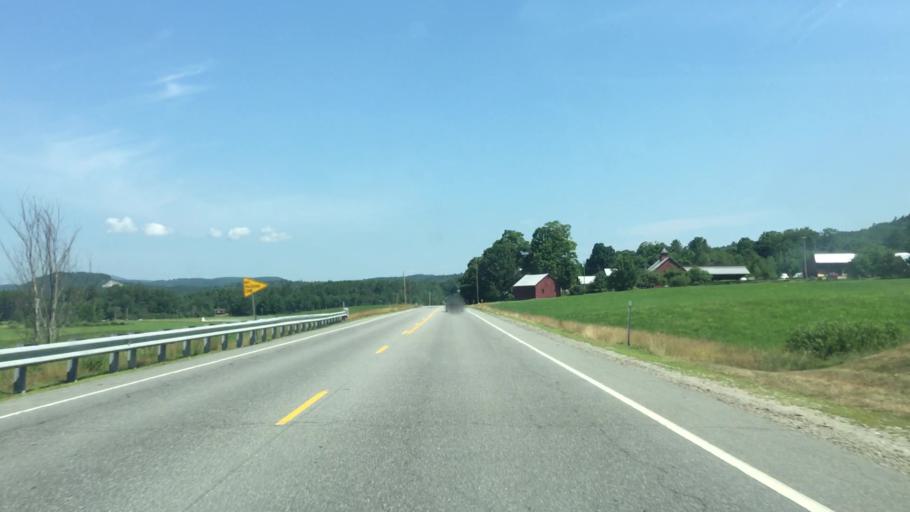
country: US
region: New Hampshire
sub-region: Sullivan County
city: Sunapee
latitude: 43.3604
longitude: -72.1196
